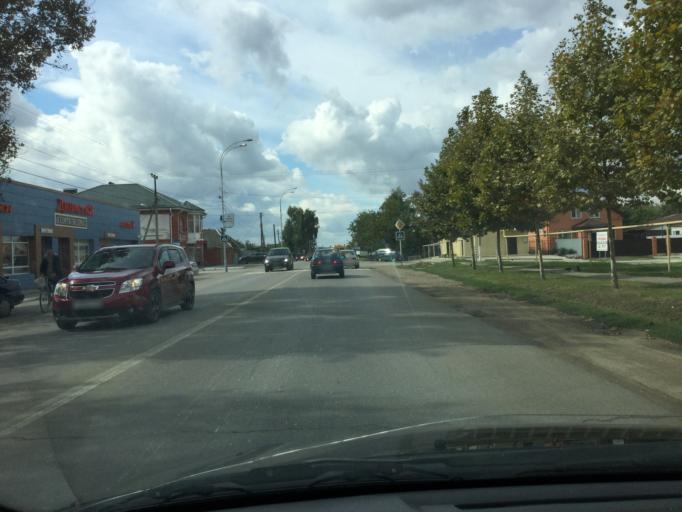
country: RU
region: Krasnodarskiy
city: Slavyansk-na-Kubani
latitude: 45.2506
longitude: 38.1034
